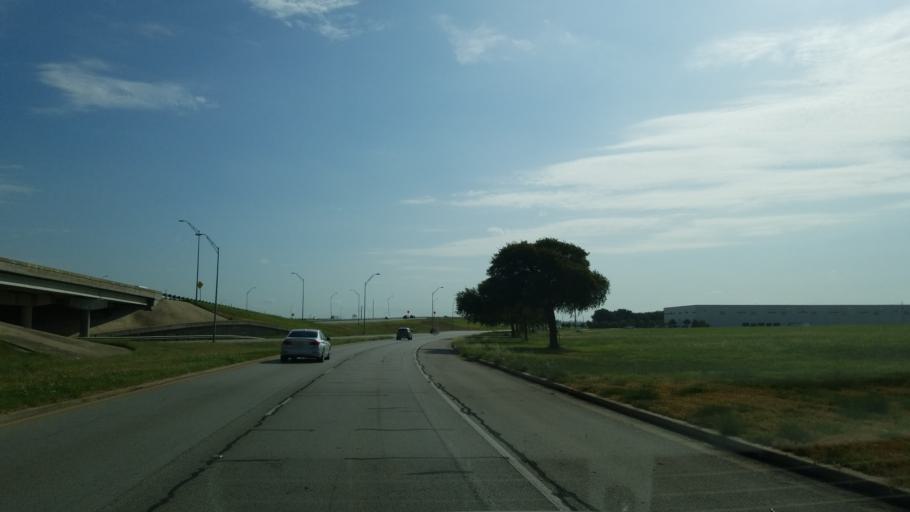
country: US
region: Texas
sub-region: Tarrant County
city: Euless
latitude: 32.8370
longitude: -97.0552
